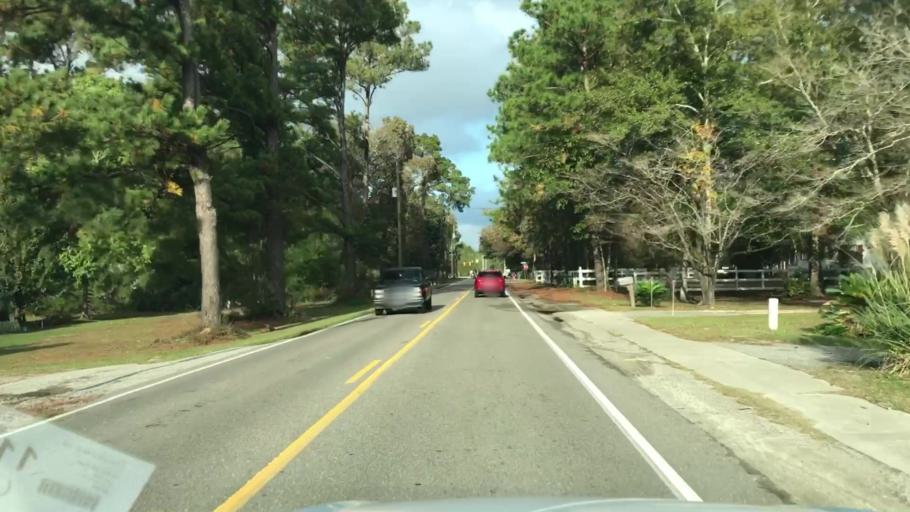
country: US
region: South Carolina
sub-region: Berkeley County
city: Sangaree
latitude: 33.0290
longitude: -80.1136
